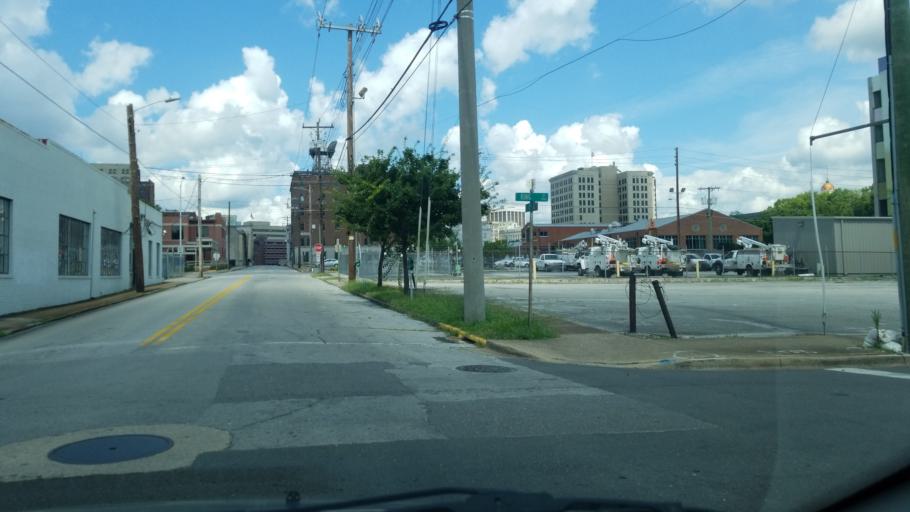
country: US
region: Tennessee
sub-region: Hamilton County
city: Chattanooga
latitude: 35.0434
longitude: -85.3054
